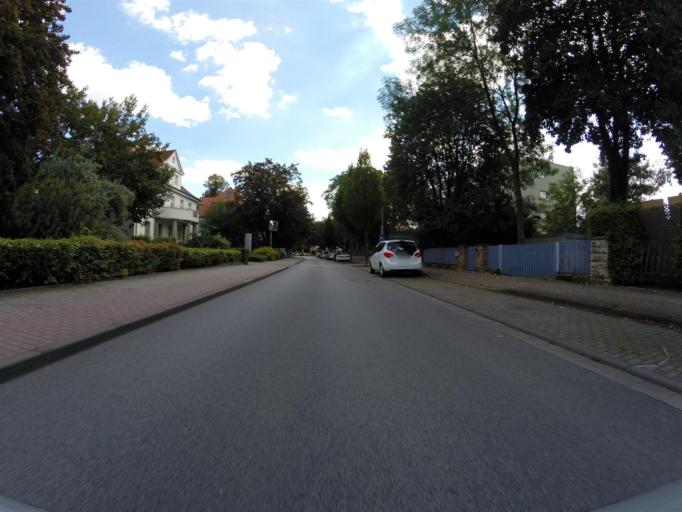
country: DE
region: Thuringia
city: Erfurt
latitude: 50.9648
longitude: 11.0146
